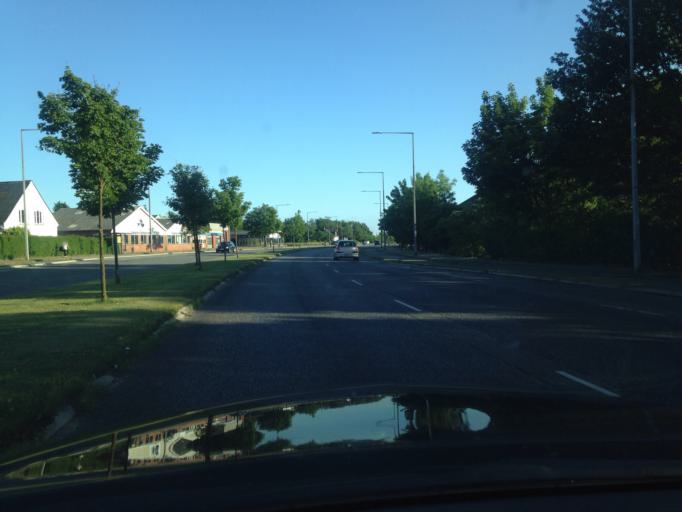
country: DK
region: South Denmark
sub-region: Kolding Kommune
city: Kolding
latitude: 55.5031
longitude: 9.4584
